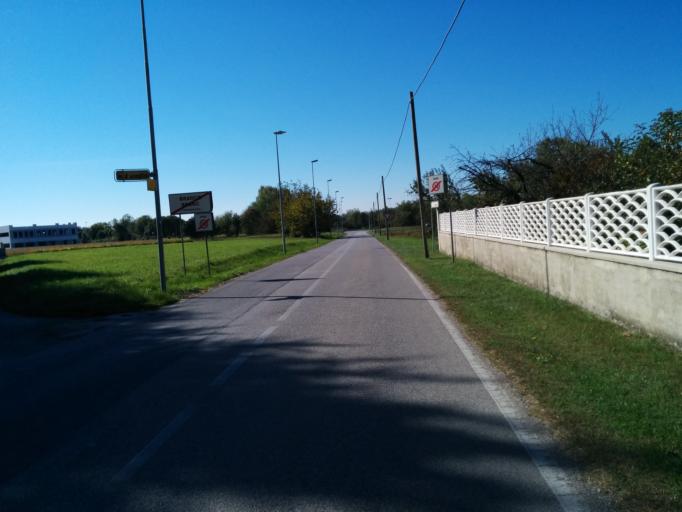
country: IT
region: Friuli Venezia Giulia
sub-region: Provincia di Udine
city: Pagnacco
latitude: 46.1140
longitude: 13.2003
